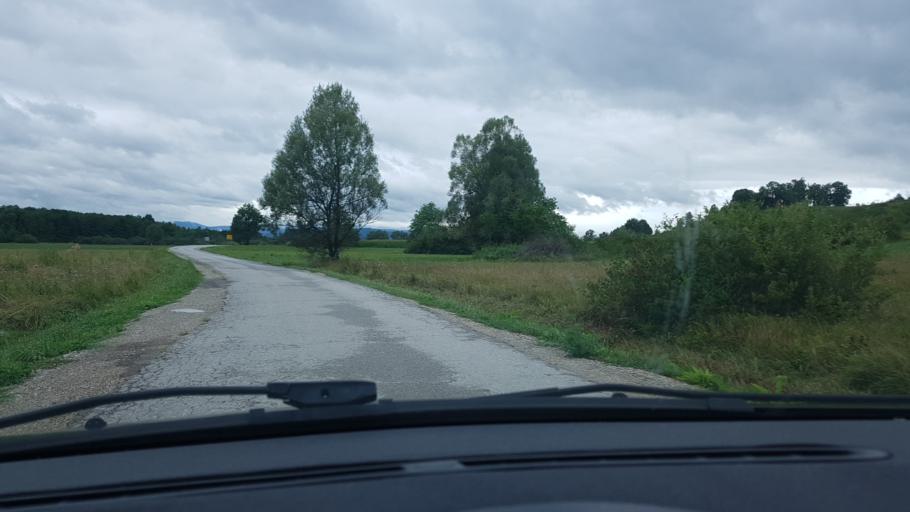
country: HR
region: Karlovacka
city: Ozalj
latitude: 45.5810
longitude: 15.5413
